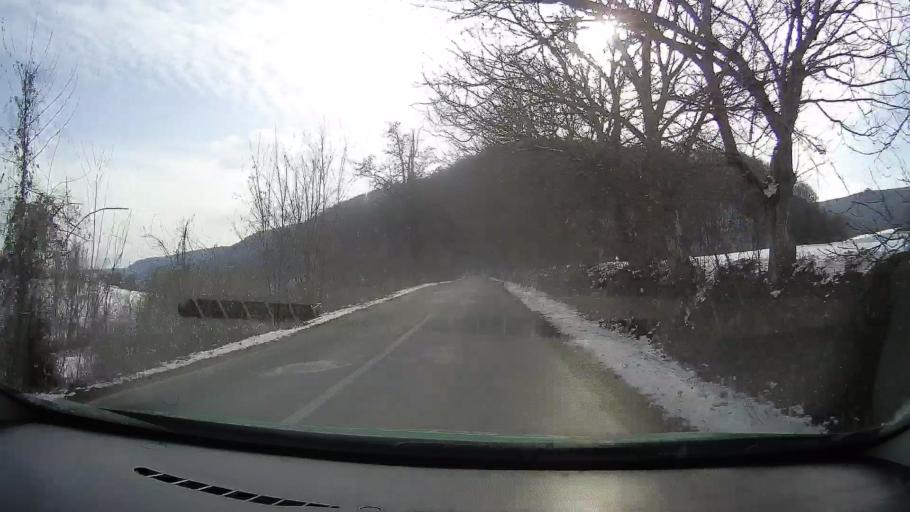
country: RO
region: Mures
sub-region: Comuna Apold
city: Saes
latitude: 46.1686
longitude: 24.7576
